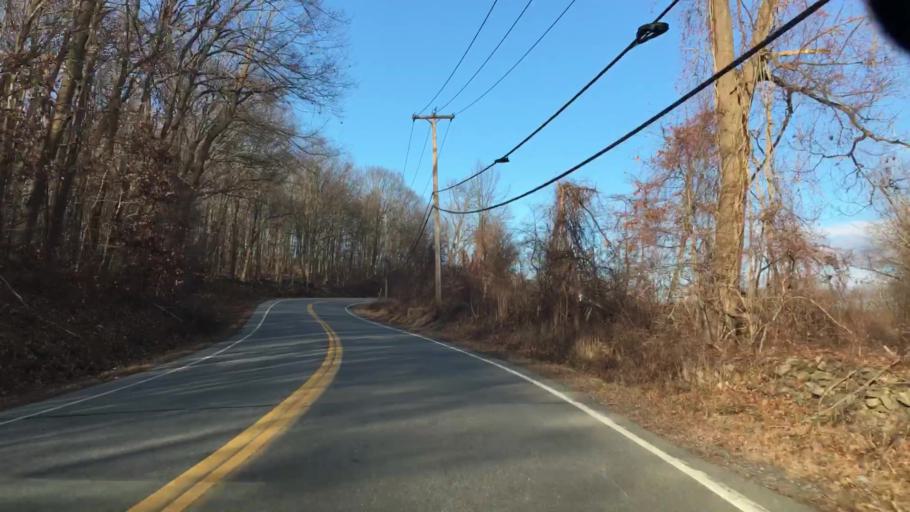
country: US
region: New York
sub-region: Putnam County
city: Lake Carmel
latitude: 41.4678
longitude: -73.6411
